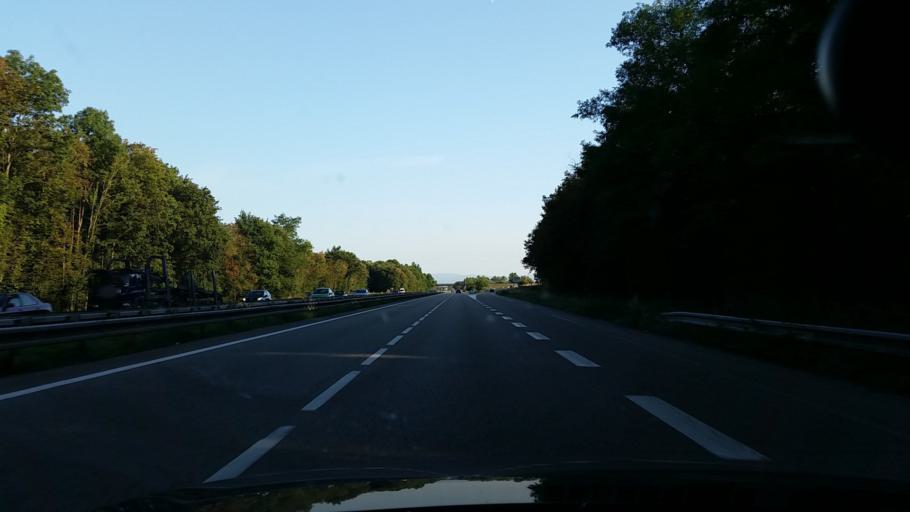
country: FR
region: Alsace
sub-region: Departement du Haut-Rhin
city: Bartenheim
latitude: 47.6416
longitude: 7.4971
